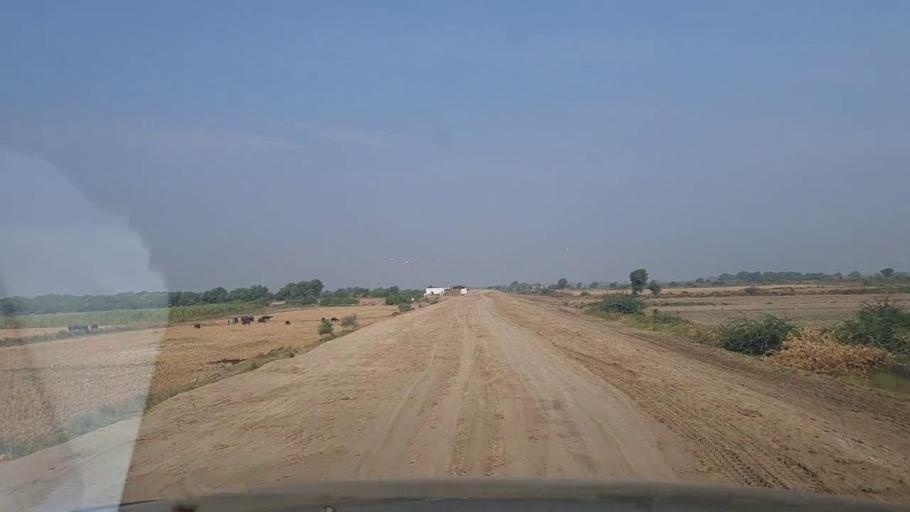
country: PK
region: Sindh
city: Bulri
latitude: 25.0009
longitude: 68.2889
